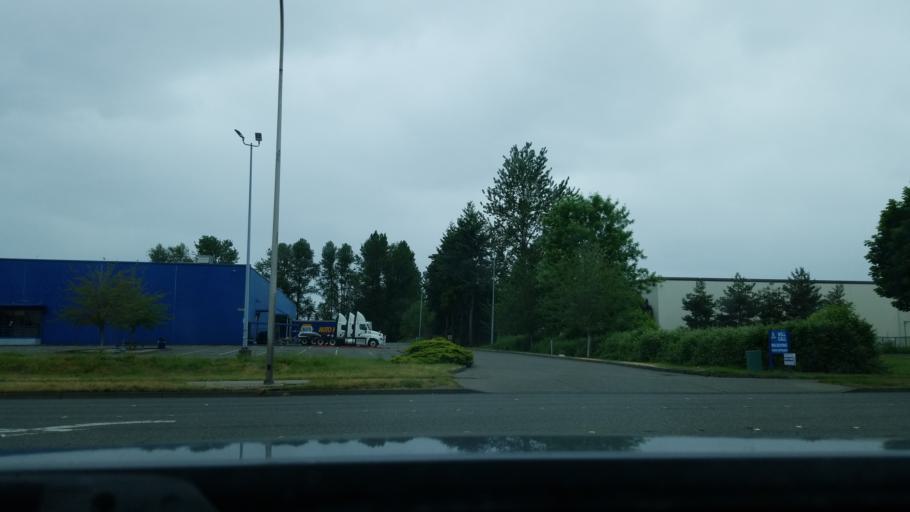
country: US
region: Washington
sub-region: King County
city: Renton
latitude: 47.4417
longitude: -122.2274
